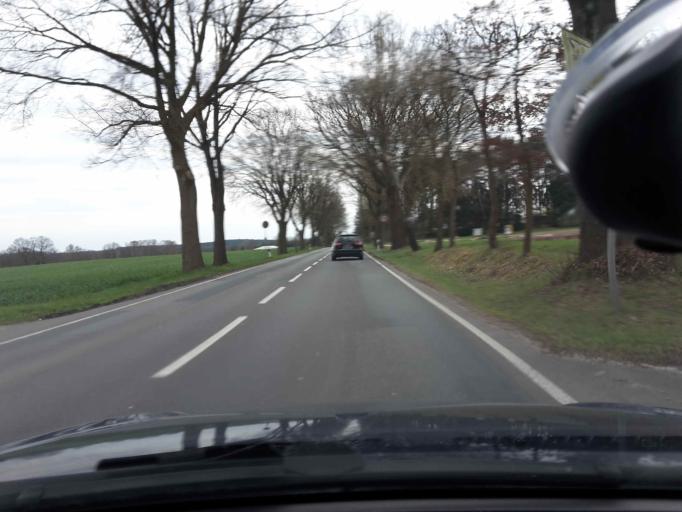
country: DE
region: Lower Saxony
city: Harmstorf
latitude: 53.3402
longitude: 9.9855
